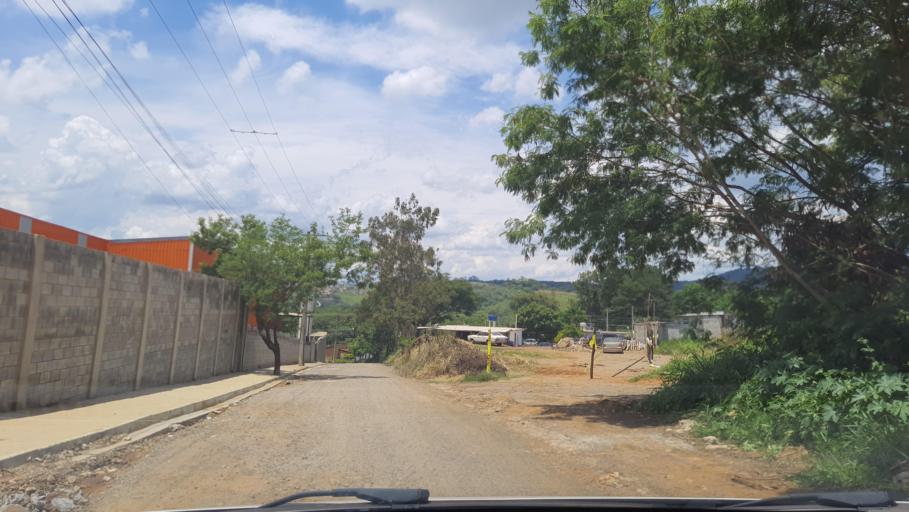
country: BR
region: Sao Paulo
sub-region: Bom Jesus Dos Perdoes
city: Bom Jesus dos Perdoes
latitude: -23.1499
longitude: -46.4601
